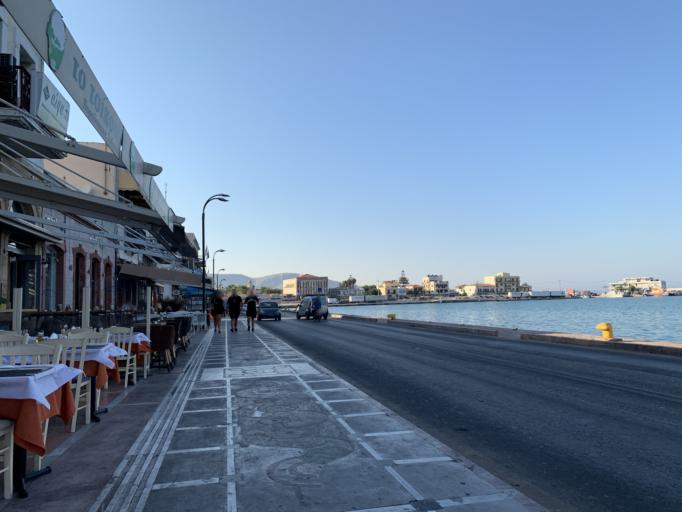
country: GR
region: North Aegean
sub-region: Chios
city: Chios
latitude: 38.3699
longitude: 26.1379
